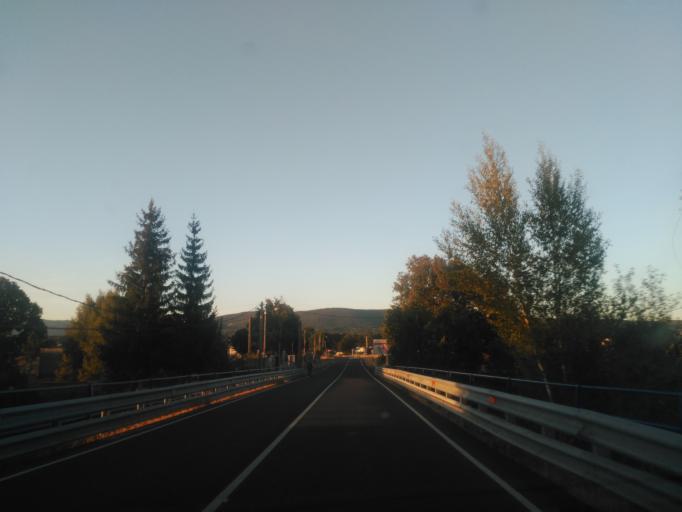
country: ES
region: Castille and Leon
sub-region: Provincia de Zamora
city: Puebla de Sanabria
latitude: 42.0586
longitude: -6.6256
